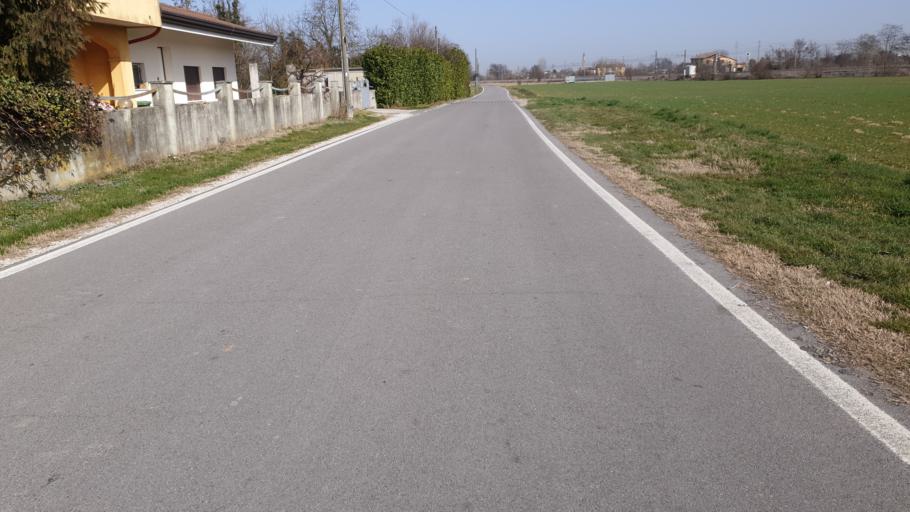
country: IT
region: Veneto
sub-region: Provincia di Padova
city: Vigodarzere
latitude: 45.4852
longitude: 11.8945
